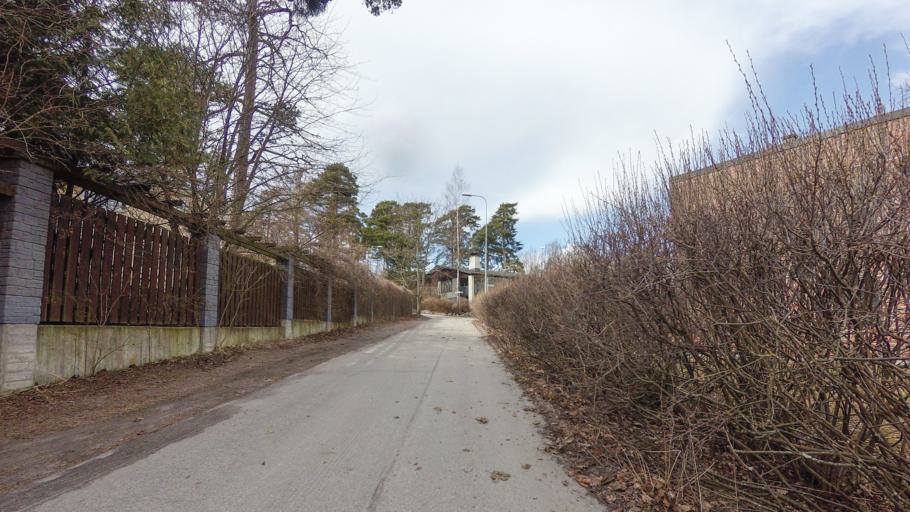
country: FI
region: Uusimaa
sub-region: Helsinki
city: Vantaa
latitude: 60.2015
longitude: 25.0963
